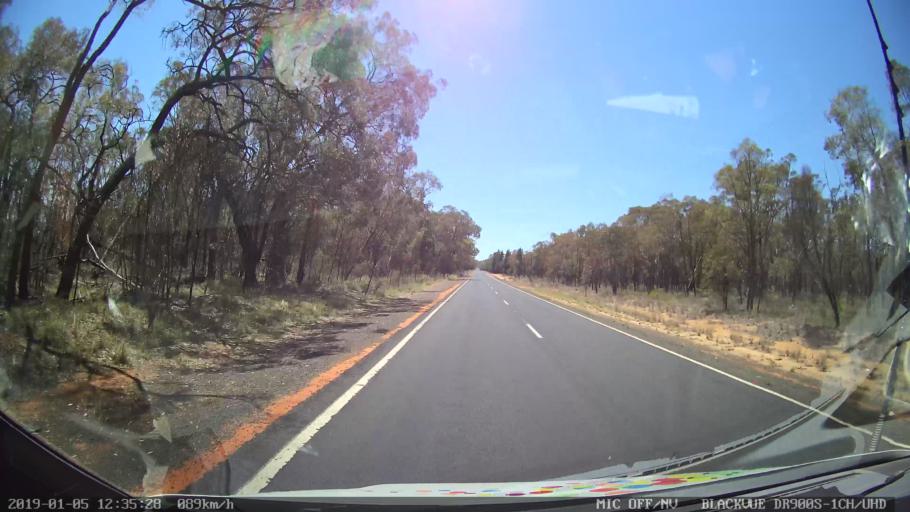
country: AU
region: New South Wales
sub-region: Warrumbungle Shire
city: Coonabarabran
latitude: -31.2095
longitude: 149.4261
